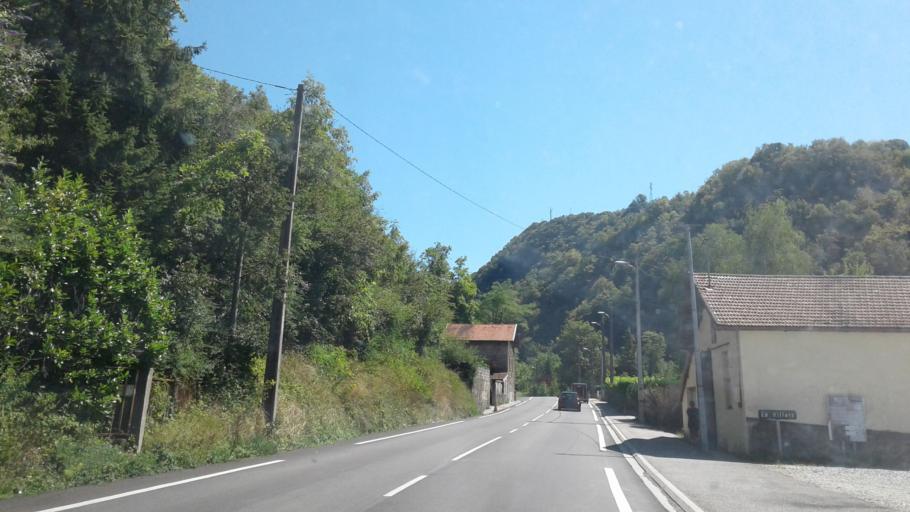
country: FR
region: Rhone-Alpes
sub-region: Departement de l'Ain
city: Tenay
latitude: 45.9297
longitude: 5.4942
